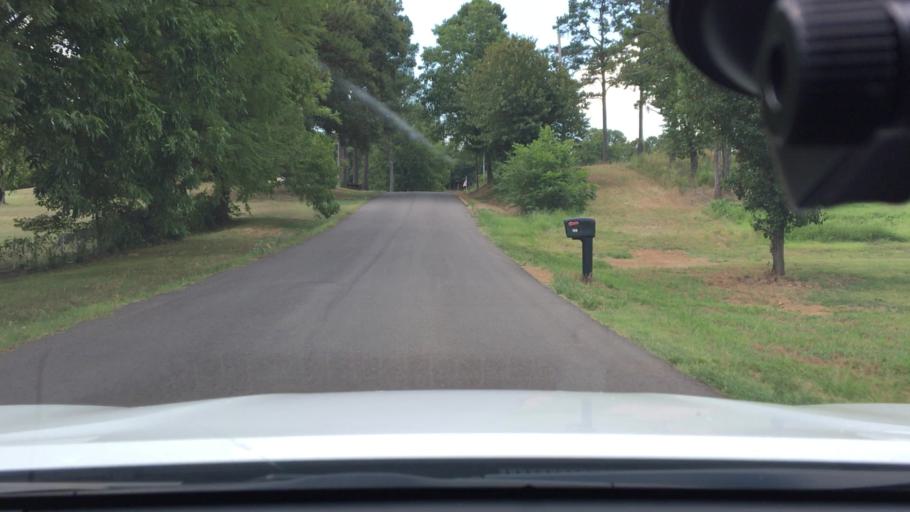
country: US
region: Arkansas
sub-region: Logan County
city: Paris
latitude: 35.2915
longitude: -93.6347
